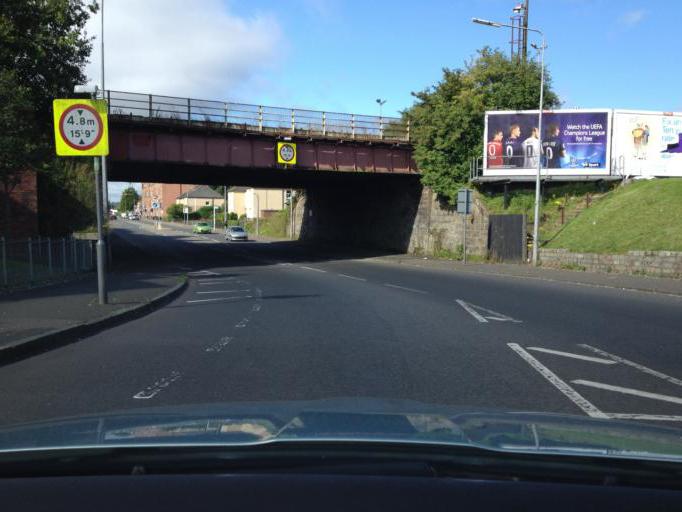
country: GB
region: Scotland
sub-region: Glasgow City
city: Glasgow
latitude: 55.8871
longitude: -4.2395
